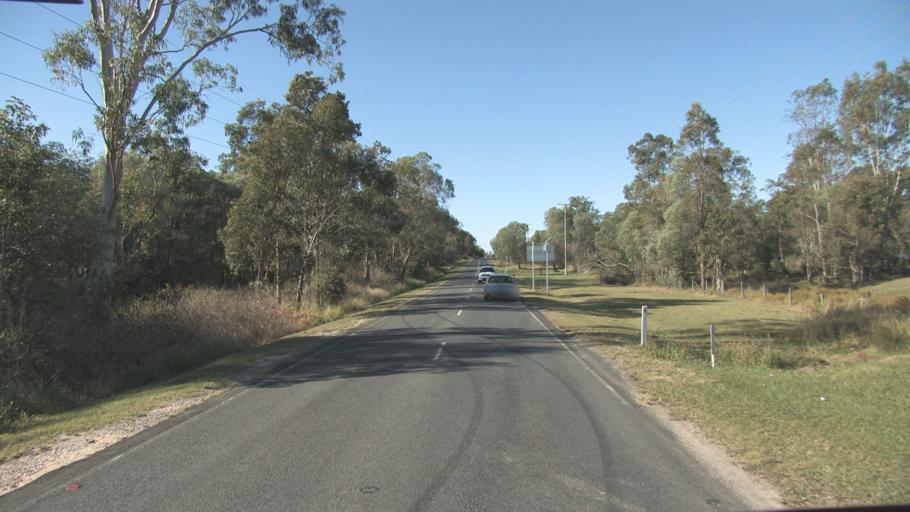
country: AU
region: Queensland
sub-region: Logan
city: North Maclean
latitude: -27.7848
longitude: 153.0503
